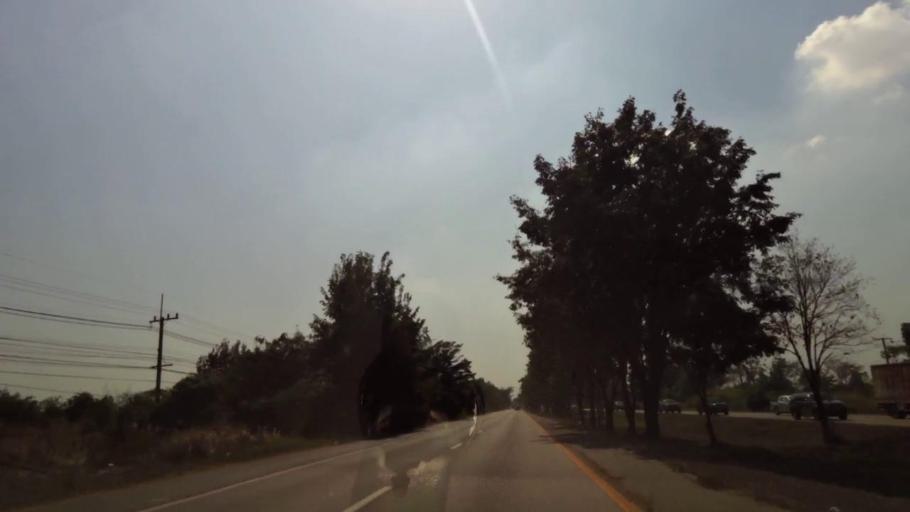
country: TH
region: Phichit
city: Wachira Barami
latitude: 16.5420
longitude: 100.1452
